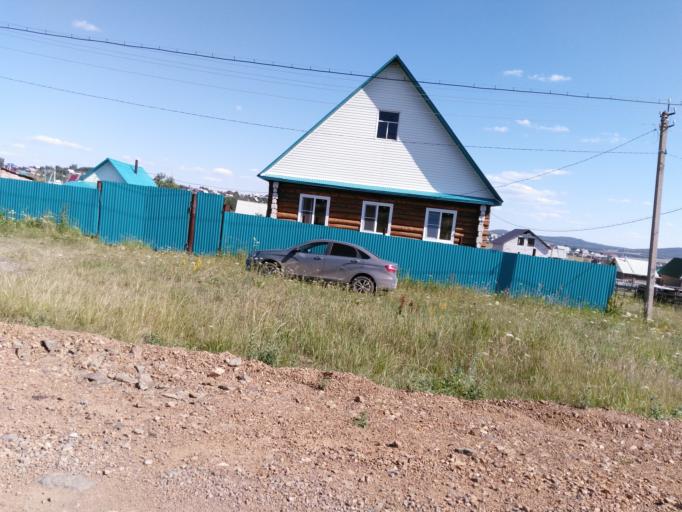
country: RU
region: Bashkortostan
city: Uchaly
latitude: 54.2924
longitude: 59.3606
